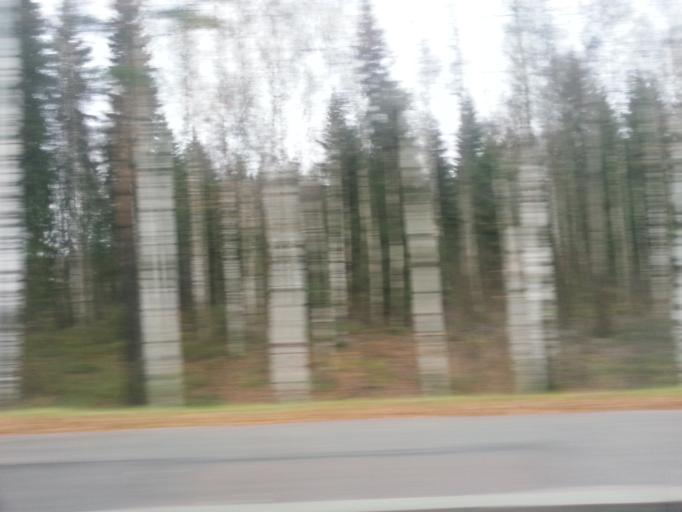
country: FI
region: Uusimaa
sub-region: Helsinki
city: Vantaa
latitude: 60.3012
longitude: 24.9514
